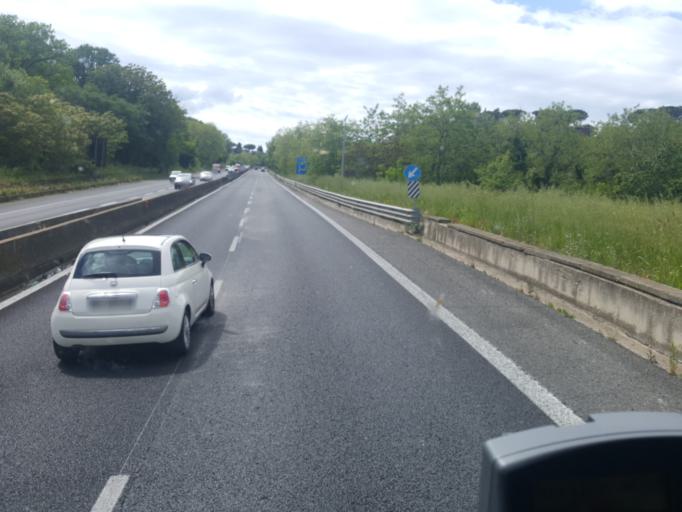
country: IT
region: Latium
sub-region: Citta metropolitana di Roma Capitale
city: Ara Nova
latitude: 41.9102
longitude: 12.2594
